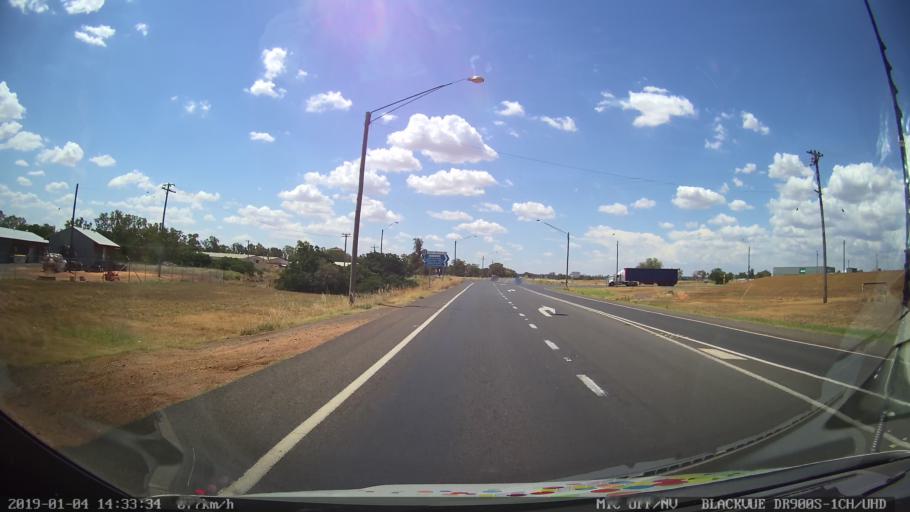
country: AU
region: New South Wales
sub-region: Dubbo Municipality
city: Dubbo
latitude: -32.2092
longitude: 148.6185
